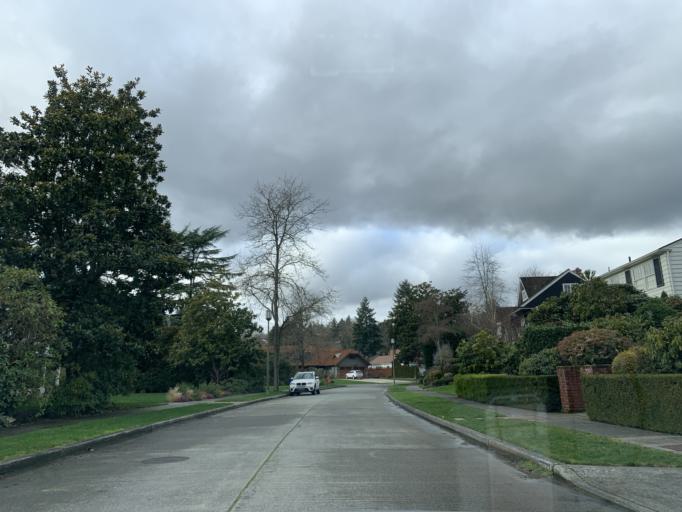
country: US
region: Washington
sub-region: King County
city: Yarrow Point
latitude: 47.6668
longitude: -122.2677
